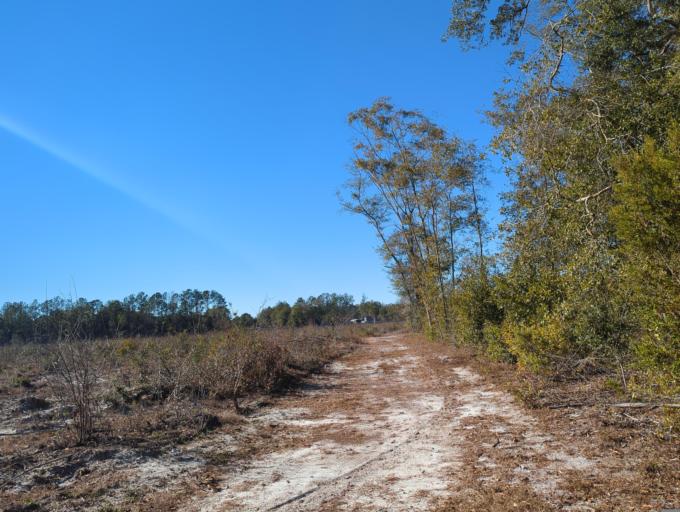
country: US
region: Florida
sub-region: Wakulla County
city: Crawfordville
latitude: 30.1837
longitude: -84.3321
